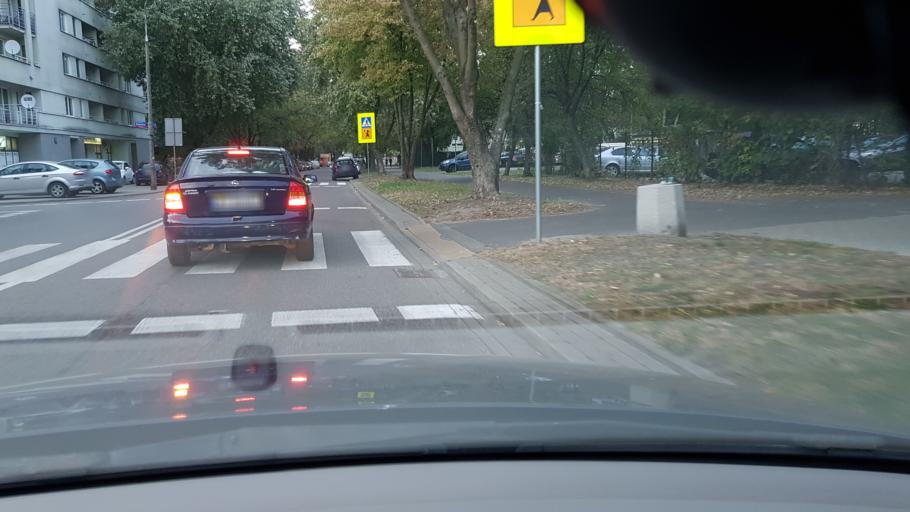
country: PL
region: Masovian Voivodeship
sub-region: Warszawa
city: Bielany
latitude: 52.2923
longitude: 20.9353
